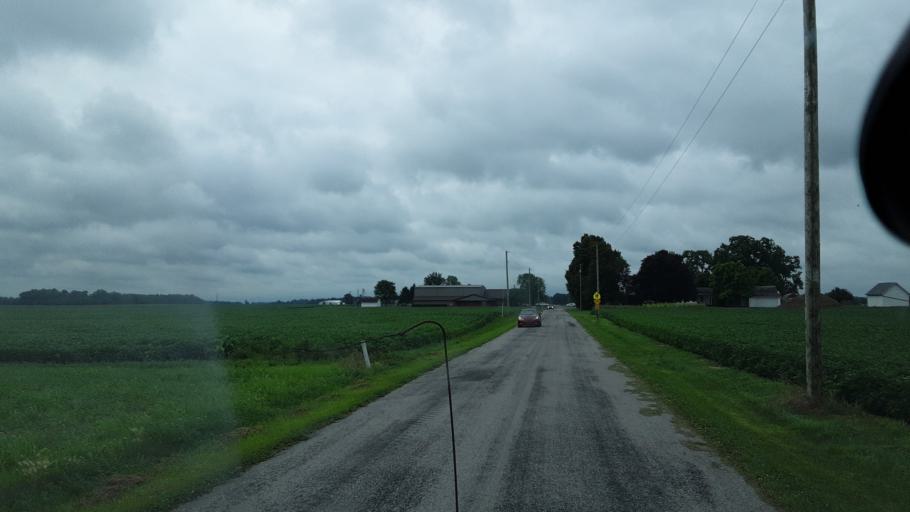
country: US
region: Indiana
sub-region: Wells County
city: Ossian
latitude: 40.8560
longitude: -85.1014
